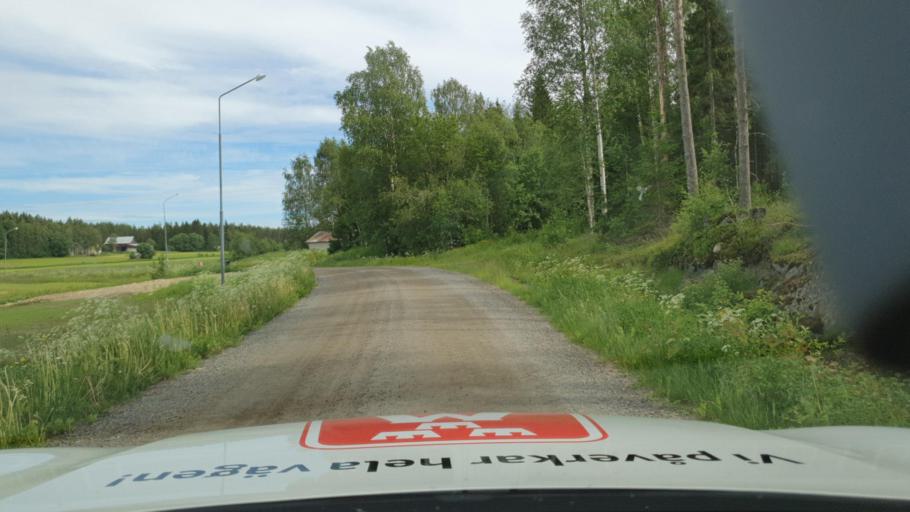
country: SE
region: Vaesterbotten
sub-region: Robertsfors Kommun
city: Robertsfors
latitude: 64.3736
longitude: 21.0429
